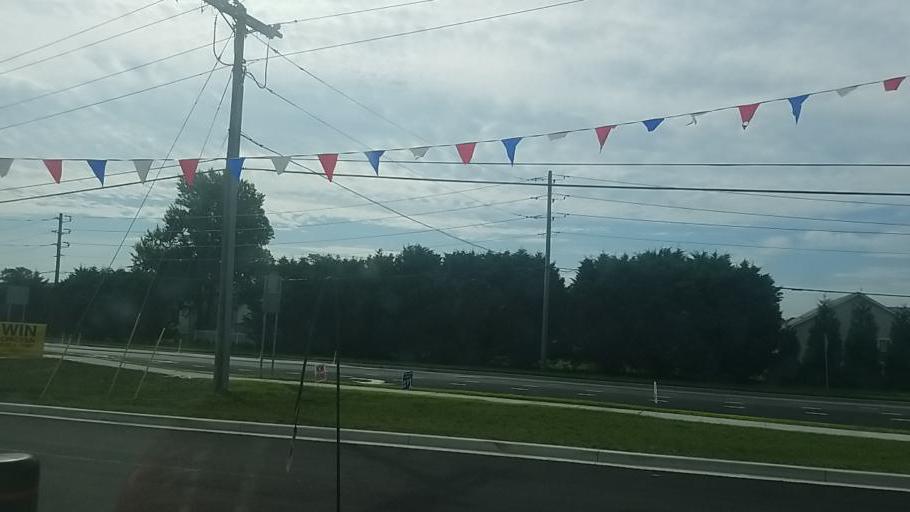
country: US
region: Delaware
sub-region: Sussex County
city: Ocean View
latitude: 38.4725
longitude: -75.1119
